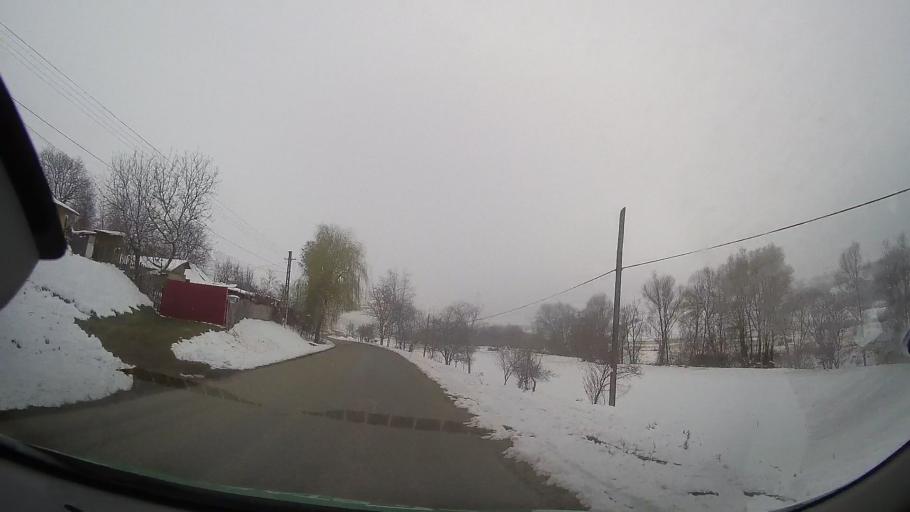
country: RO
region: Bacau
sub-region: Comuna Vultureni
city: Vultureni
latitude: 46.3824
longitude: 27.2764
